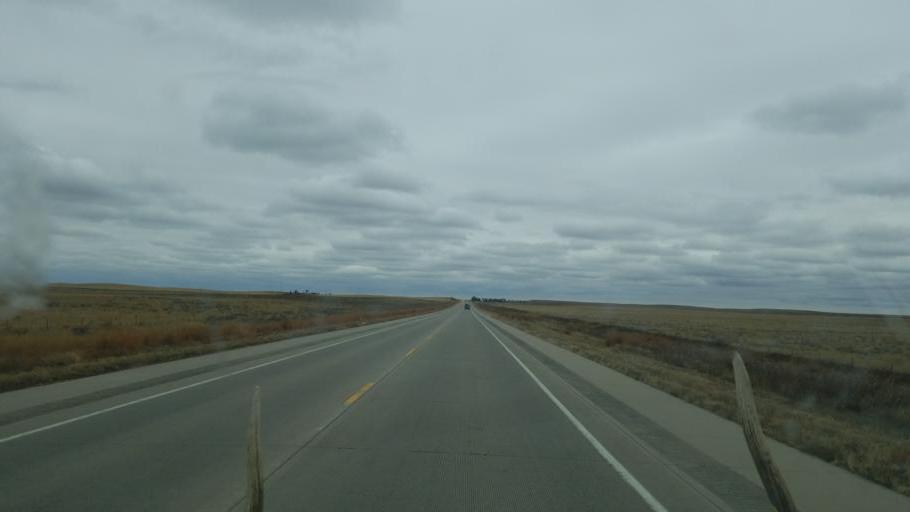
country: US
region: Colorado
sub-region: Kiowa County
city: Eads
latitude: 38.7101
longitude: -102.7758
